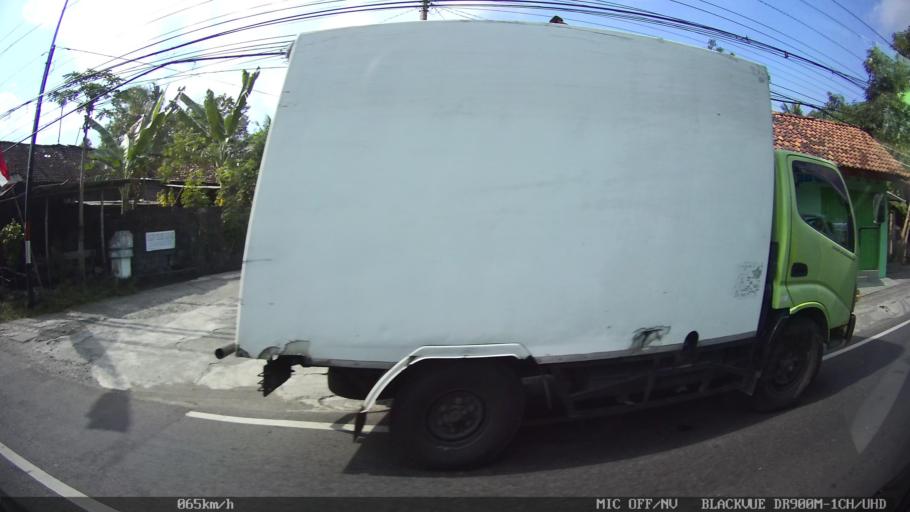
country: ID
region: Daerah Istimewa Yogyakarta
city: Godean
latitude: -7.8160
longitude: 110.2506
